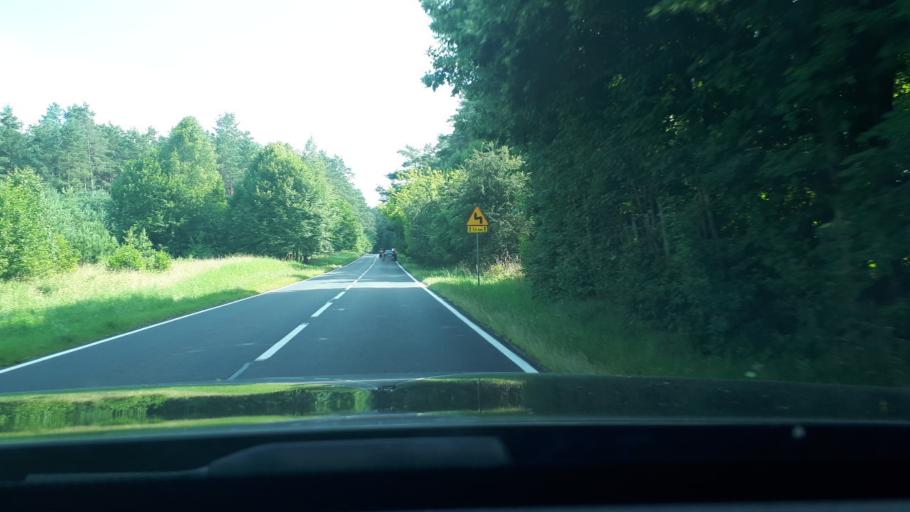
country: PL
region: Warmian-Masurian Voivodeship
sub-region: Powiat olsztynski
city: Stawiguda
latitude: 53.5443
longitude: 20.4199
